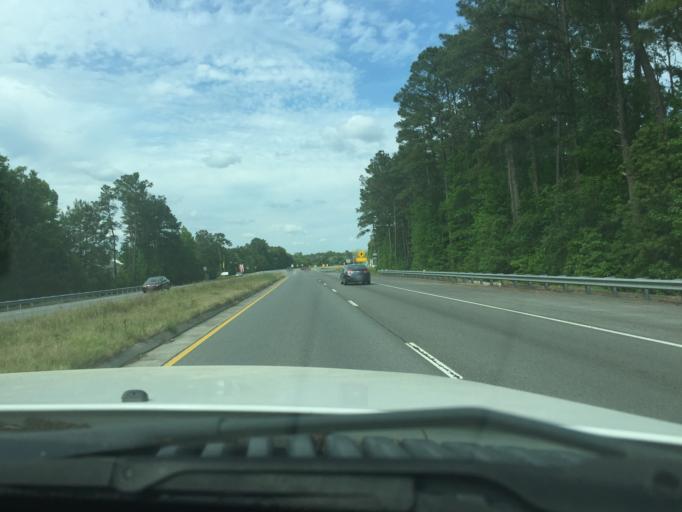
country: US
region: Georgia
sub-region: Chatham County
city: Georgetown
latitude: 31.9910
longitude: -81.2763
